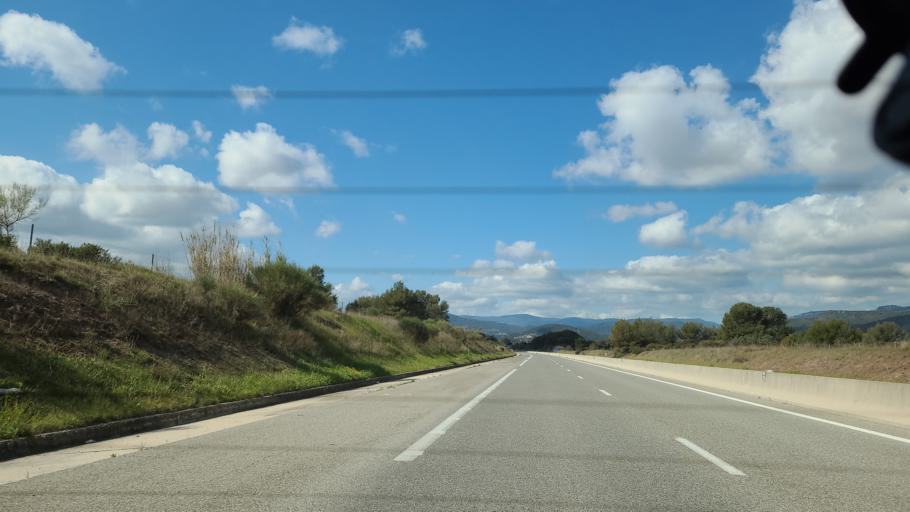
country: FR
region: Provence-Alpes-Cote d'Azur
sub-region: Departement du Var
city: Puget-Ville
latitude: 43.2622
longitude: 6.1352
